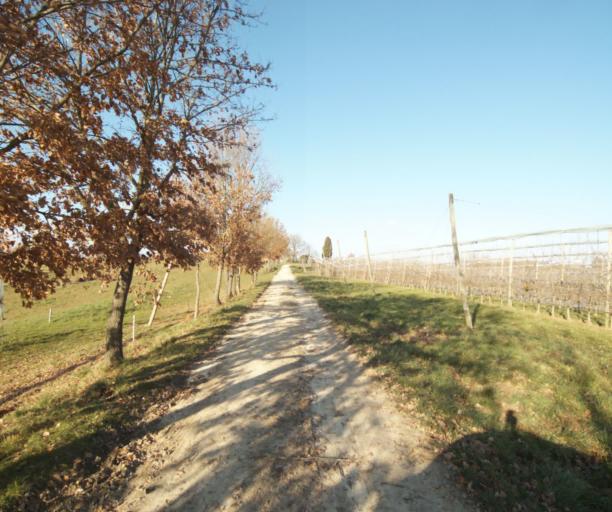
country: FR
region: Midi-Pyrenees
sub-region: Departement du Tarn-et-Garonne
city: Moissac
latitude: 44.1360
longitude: 1.0482
